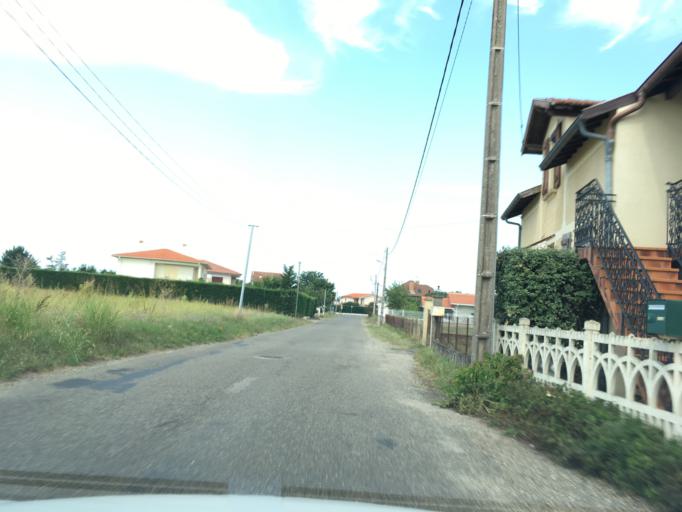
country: FR
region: Midi-Pyrenees
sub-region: Departement du Tarn-et-Garonne
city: Montbeton
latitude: 44.0135
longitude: 1.3205
